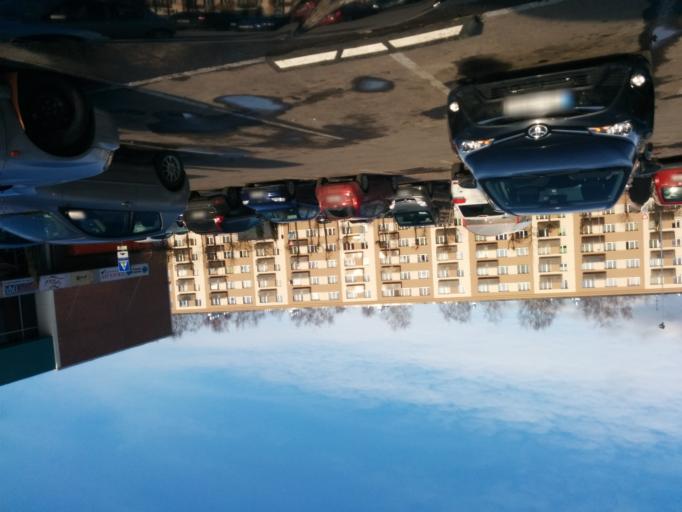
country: LV
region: Jelgava
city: Jelgava
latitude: 56.6481
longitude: 23.7257
